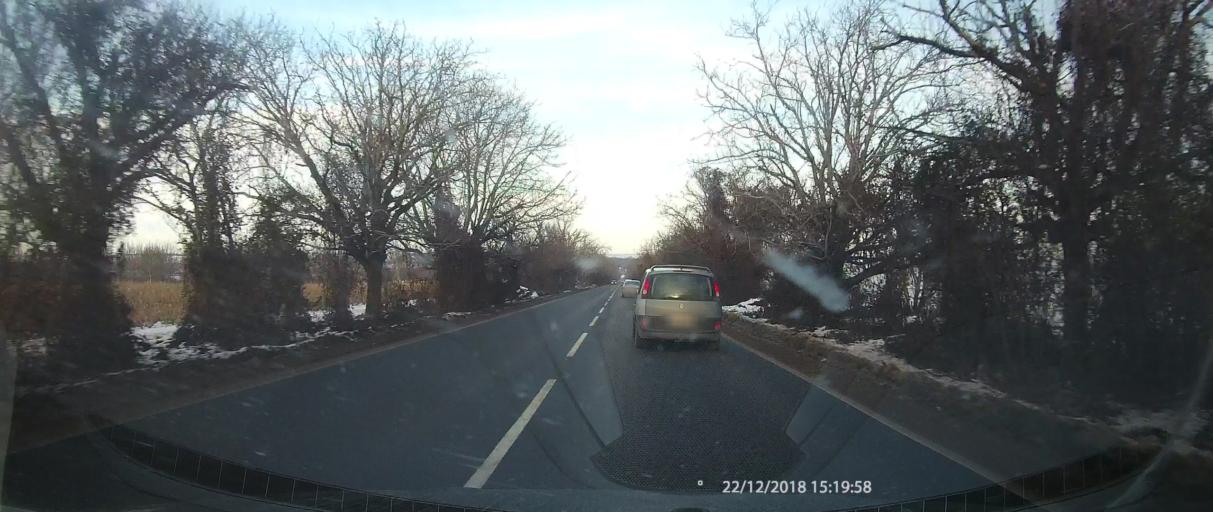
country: BG
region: Ruse
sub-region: Obshtina Dve Mogili
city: Dve Mogili
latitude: 43.6645
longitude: 25.8806
